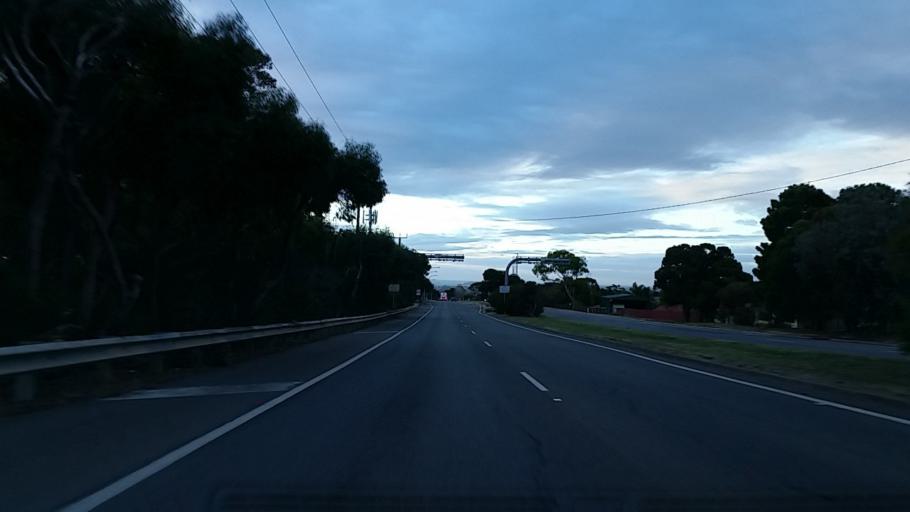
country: AU
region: South Australia
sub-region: Adelaide Hills
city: Seacliff
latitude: -35.0453
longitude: 138.5313
